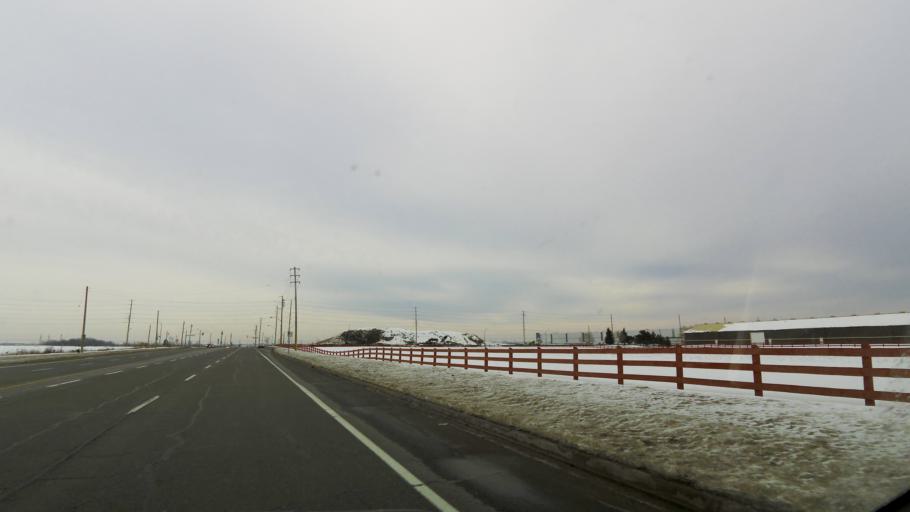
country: CA
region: Ontario
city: Brampton
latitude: 43.7859
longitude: -79.6540
